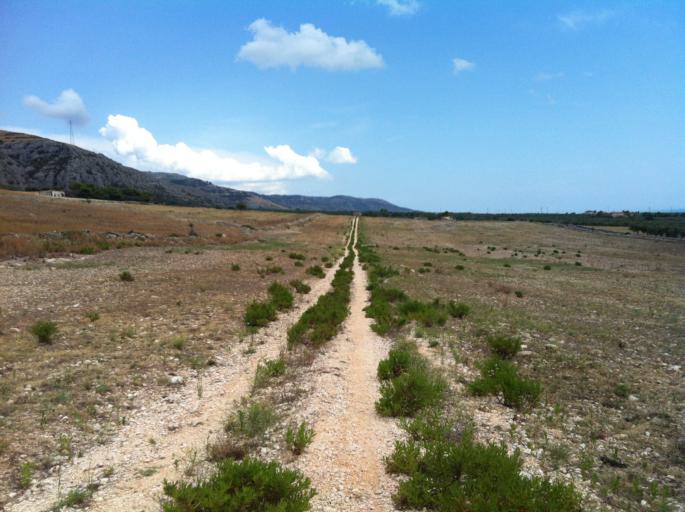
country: IT
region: Apulia
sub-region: Provincia di Foggia
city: Manfredonia
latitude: 41.6607
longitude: 15.9315
